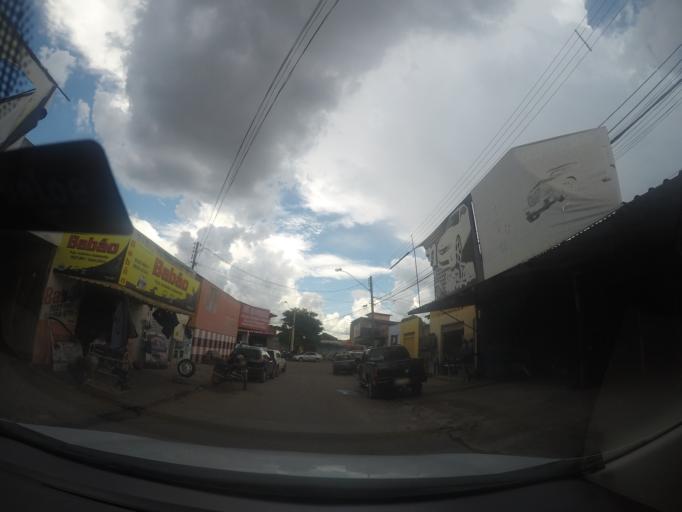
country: BR
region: Goias
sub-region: Goiania
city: Goiania
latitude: -16.6934
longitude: -49.3160
